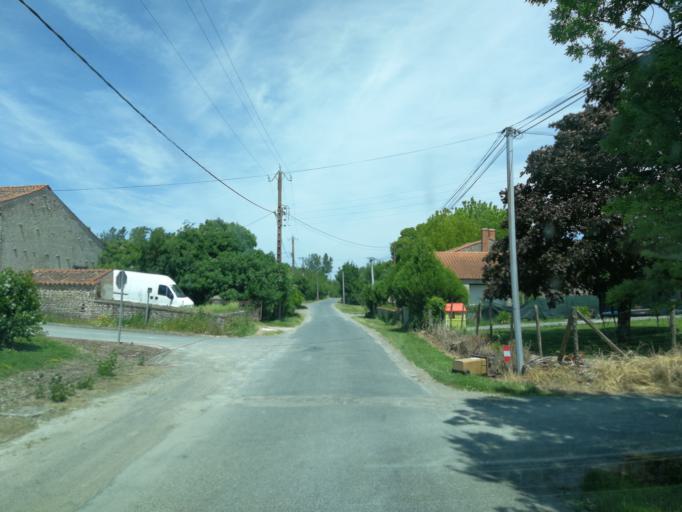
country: FR
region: Pays de la Loire
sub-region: Departement de la Vendee
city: Le Langon
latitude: 46.3856
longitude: -0.9403
